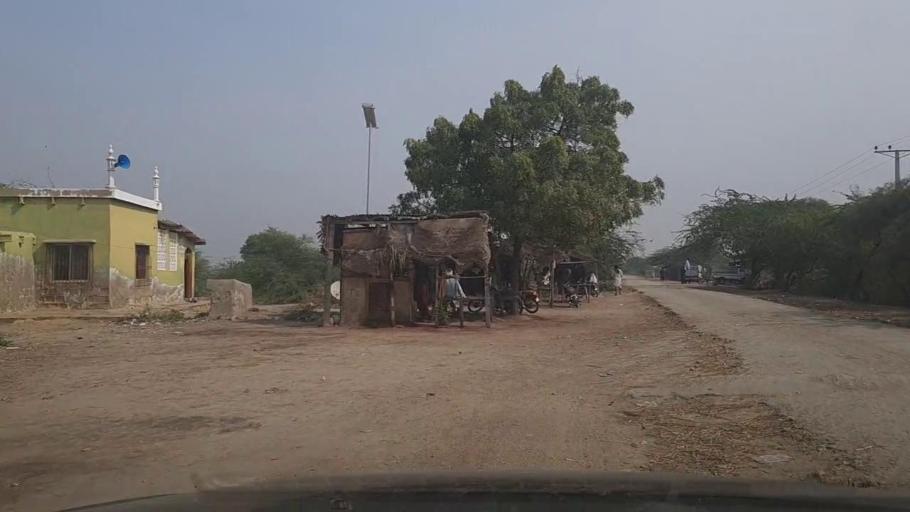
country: PK
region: Sindh
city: Mirpur Sakro
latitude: 24.4796
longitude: 67.6474
